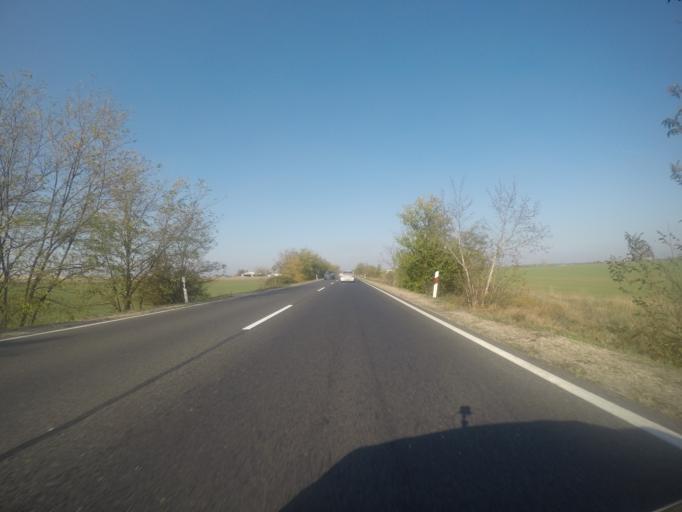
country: HU
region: Fejer
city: Baracs
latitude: 46.8900
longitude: 18.9204
